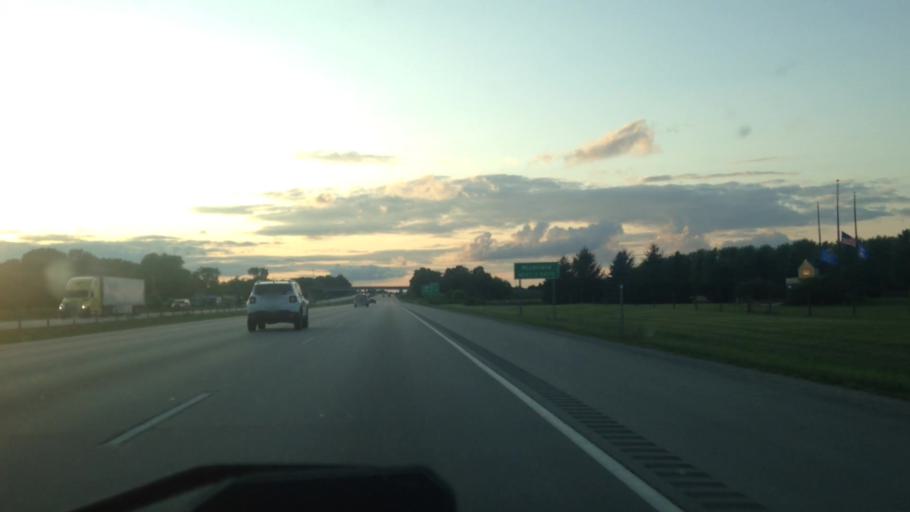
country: US
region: Wisconsin
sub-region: Washington County
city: Richfield
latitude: 43.2316
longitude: -88.1682
